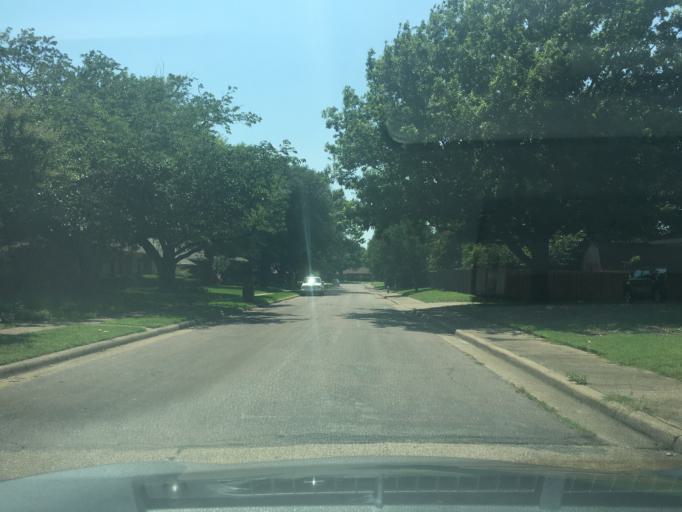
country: US
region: Texas
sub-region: Dallas County
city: Richardson
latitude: 32.9301
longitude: -96.7093
